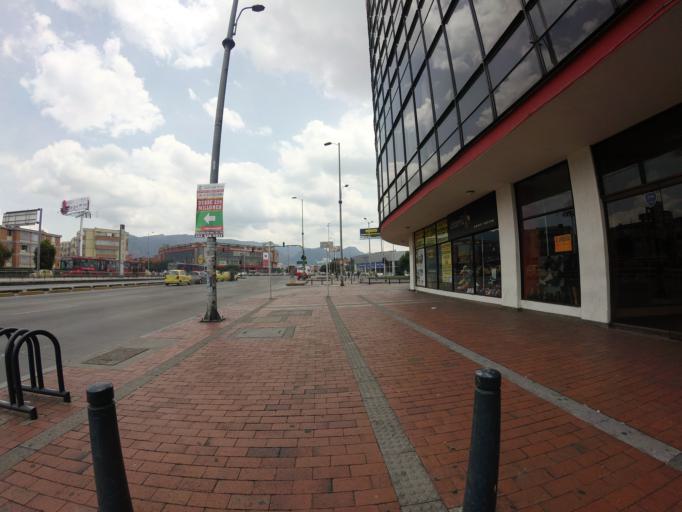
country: CO
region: Bogota D.C.
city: Barrio San Luis
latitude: 4.6899
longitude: -74.0656
